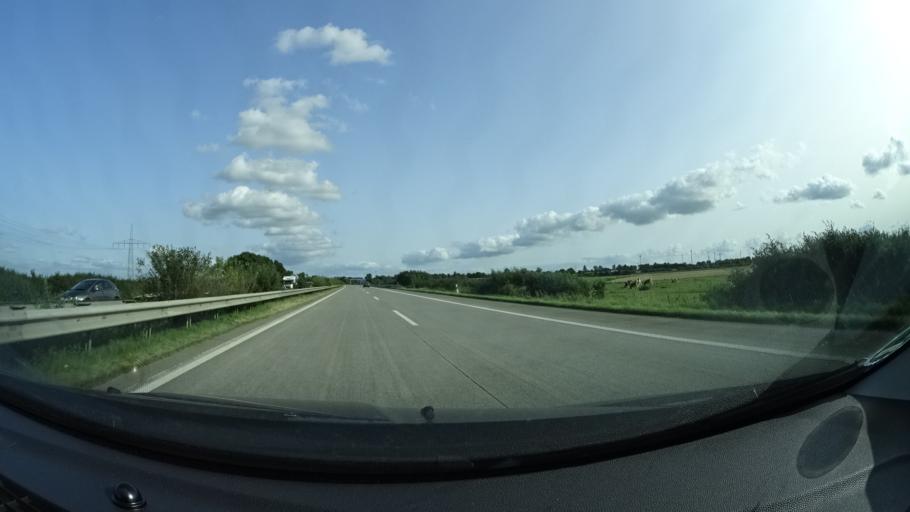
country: DE
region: Schleswig-Holstein
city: Rethwisch
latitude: 53.8527
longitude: 9.5825
